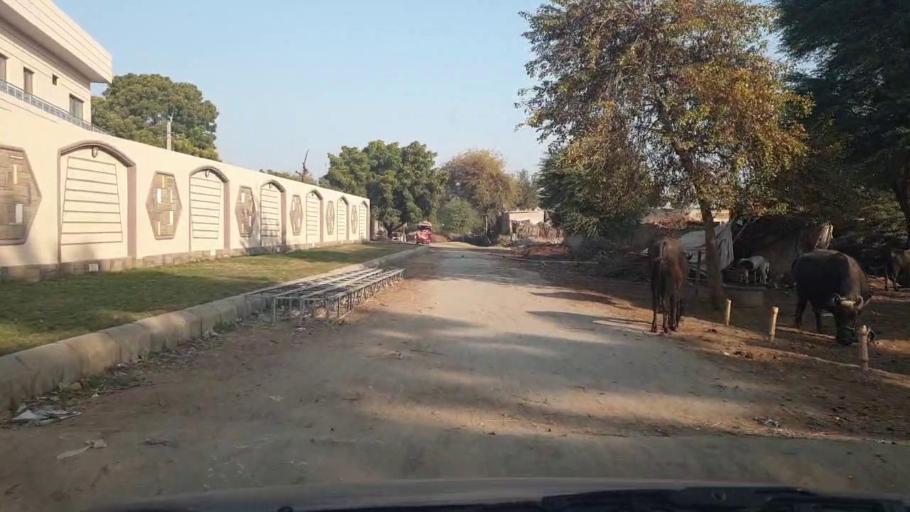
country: PK
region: Sindh
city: Tando Adam
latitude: 25.7529
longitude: 68.6404
